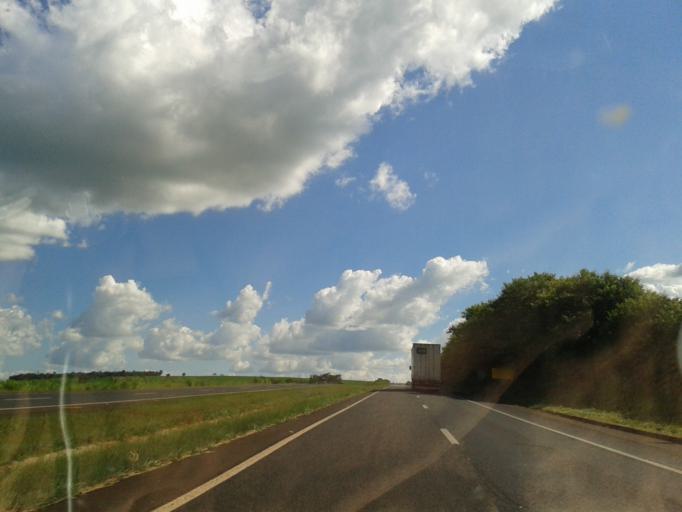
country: BR
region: Goias
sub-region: Goiatuba
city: Goiatuba
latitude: -18.0109
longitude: -49.2621
